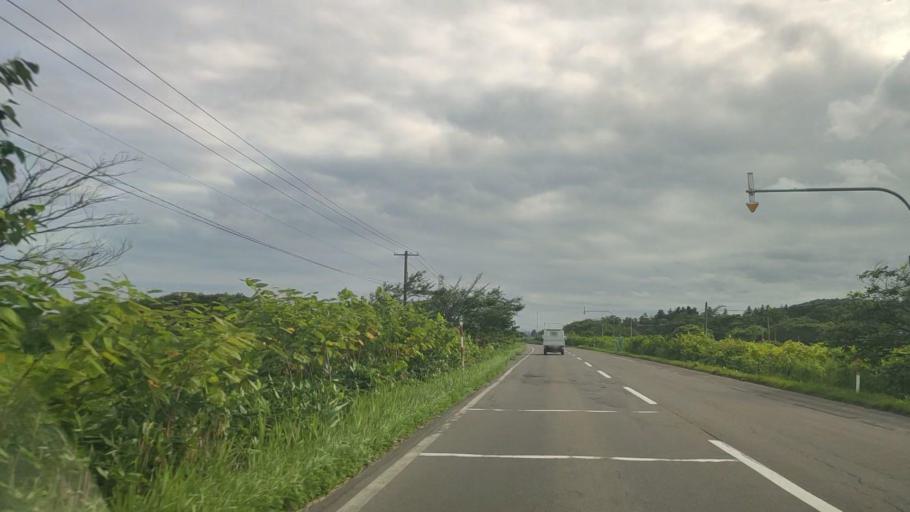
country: JP
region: Hokkaido
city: Niseko Town
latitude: 42.4597
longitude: 140.3358
